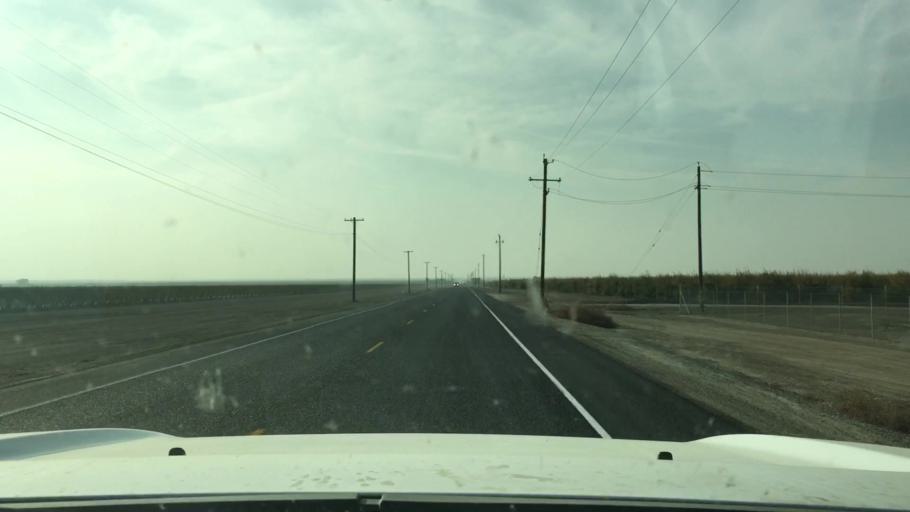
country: US
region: California
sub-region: Kern County
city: Lost Hills
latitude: 35.4995
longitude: -119.6060
